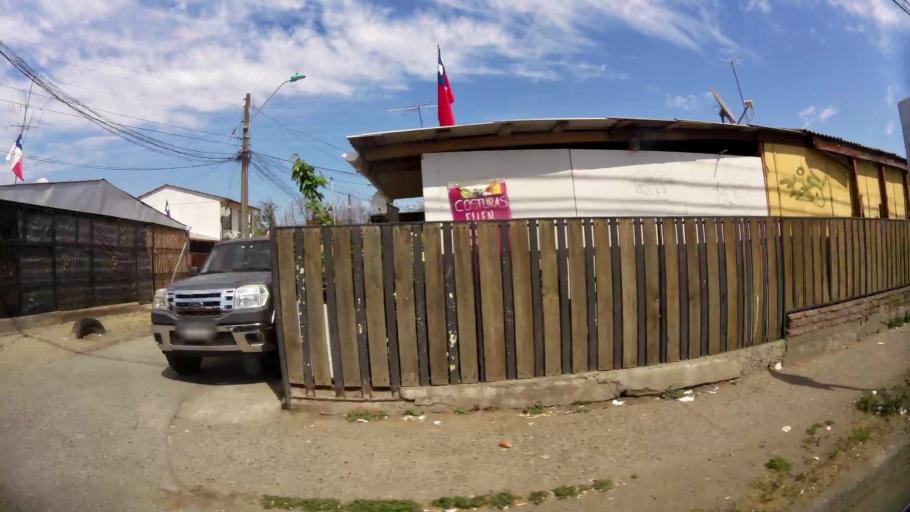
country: CL
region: Santiago Metropolitan
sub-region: Provincia de Talagante
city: Talagante
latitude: -33.6646
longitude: -70.9194
